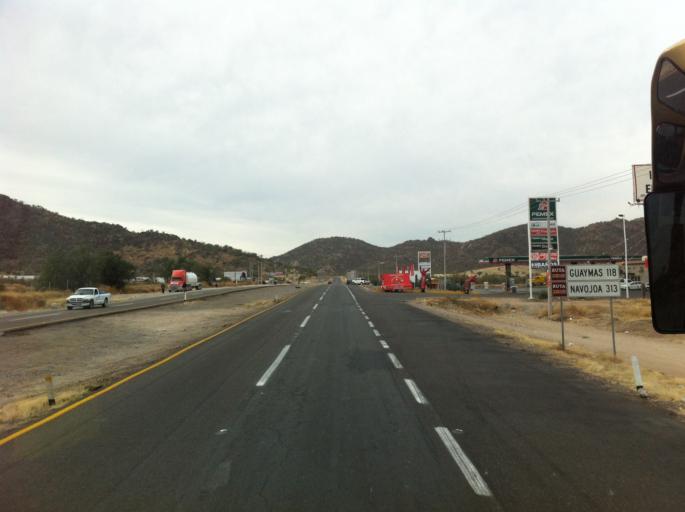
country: MX
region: Sonora
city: Hermosillo
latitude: 29.0013
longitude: -110.9684
